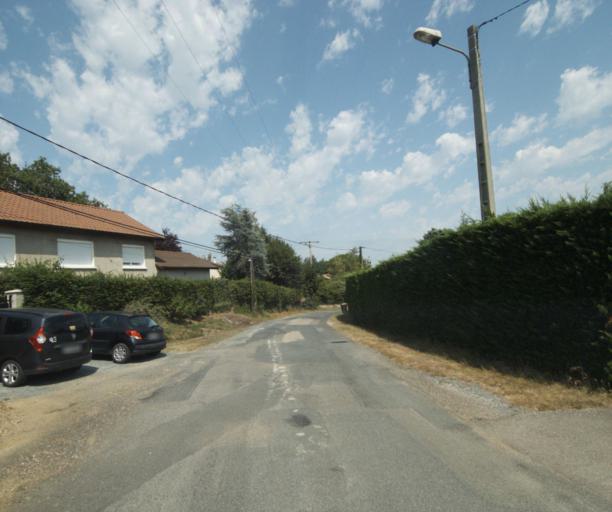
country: FR
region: Rhone-Alpes
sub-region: Departement du Rhone
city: Lentilly
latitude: 45.8434
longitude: 4.6599
